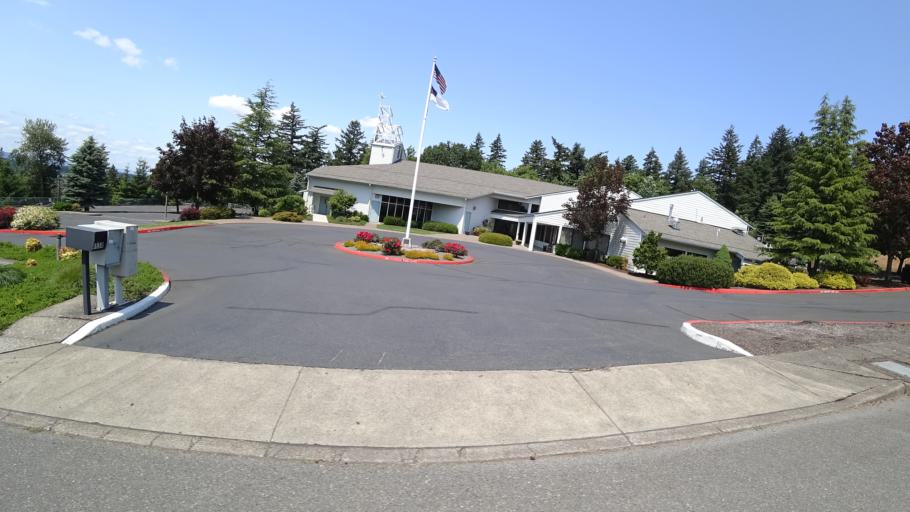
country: US
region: Oregon
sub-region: Multnomah County
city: Lents
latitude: 45.4514
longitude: -122.5678
